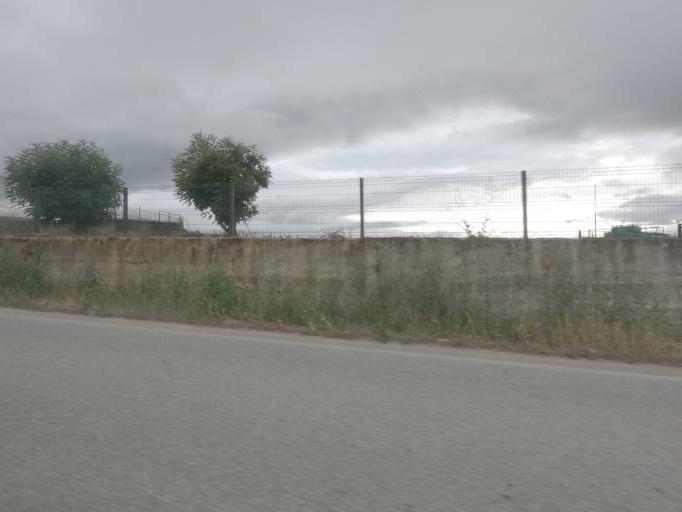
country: PT
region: Vila Real
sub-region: Sabrosa
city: Sabrosa
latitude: 41.2805
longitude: -7.5126
